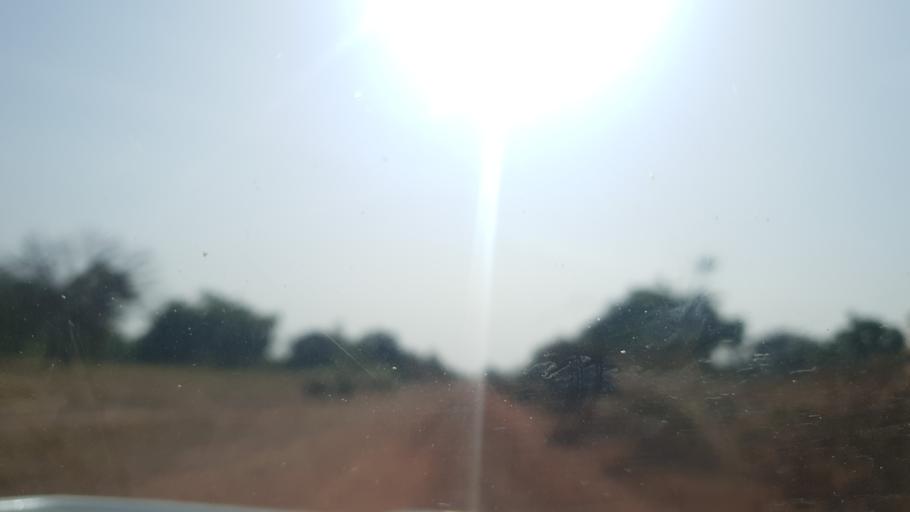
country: ML
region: Koulikoro
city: Dioila
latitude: 12.7025
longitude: -6.7653
